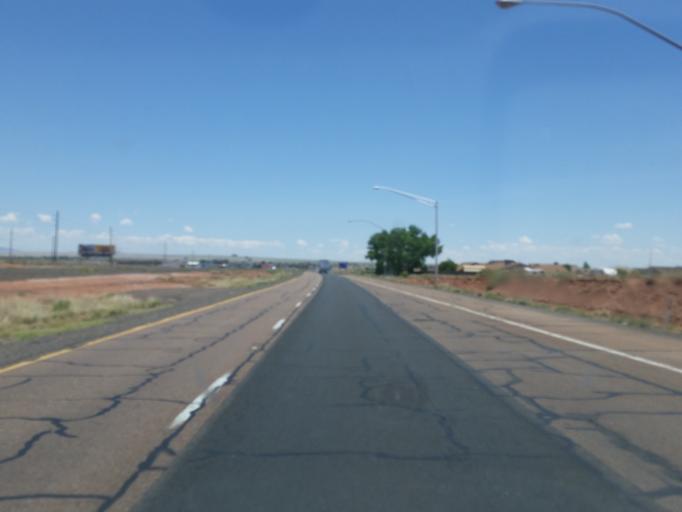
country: US
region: Arizona
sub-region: Navajo County
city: Winslow
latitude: 35.0379
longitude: -110.7187
